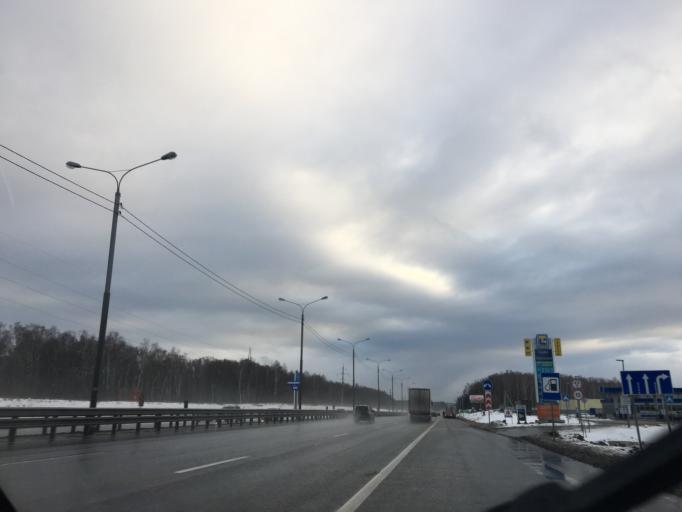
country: RU
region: Moskovskaya
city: Lyubuchany
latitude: 55.2798
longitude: 37.5400
